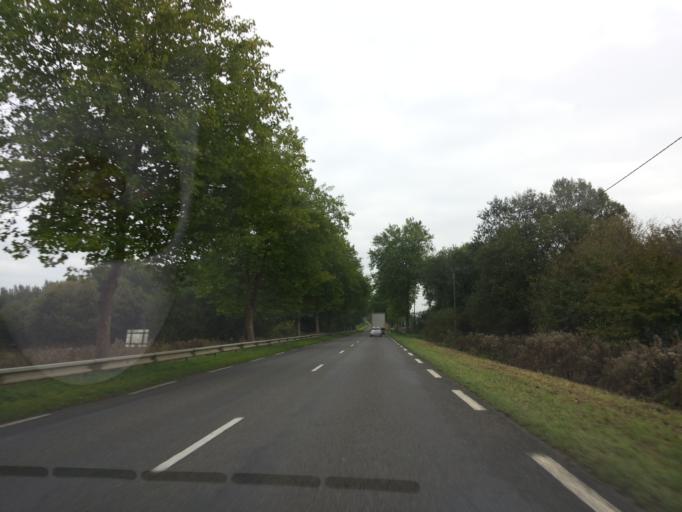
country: FR
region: Champagne-Ardenne
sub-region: Departement des Ardennes
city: Pouru-Saint-Remy
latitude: 49.6752
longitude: 5.0955
